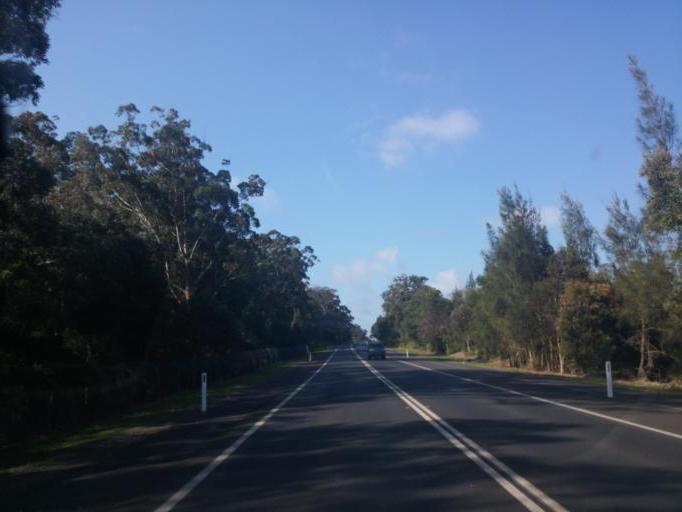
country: AU
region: New South Wales
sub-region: Coffs Harbour
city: Coffs Harbour
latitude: -30.2986
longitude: 153.1273
